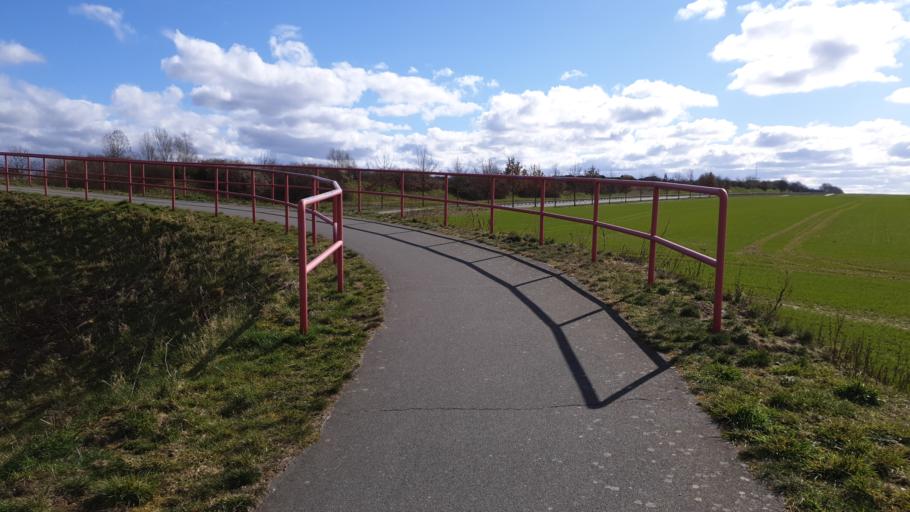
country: DE
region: Mecklenburg-Vorpommern
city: Lankow
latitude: 53.6397
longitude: 11.3505
